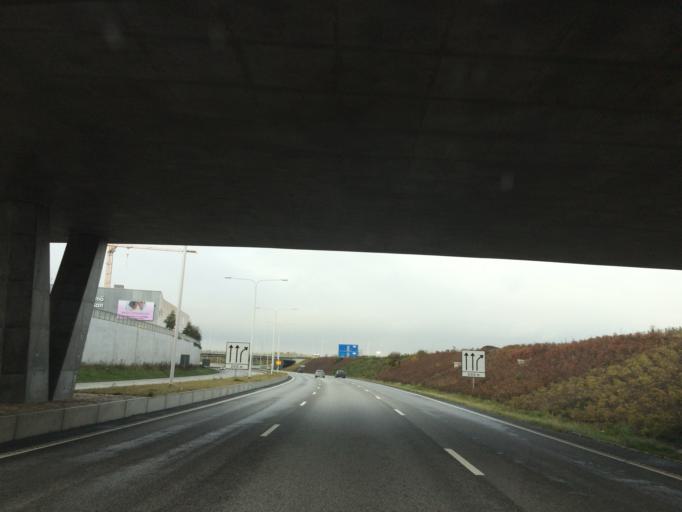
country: SE
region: Skane
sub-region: Malmo
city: Malmoe
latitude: 55.5683
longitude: 12.9808
